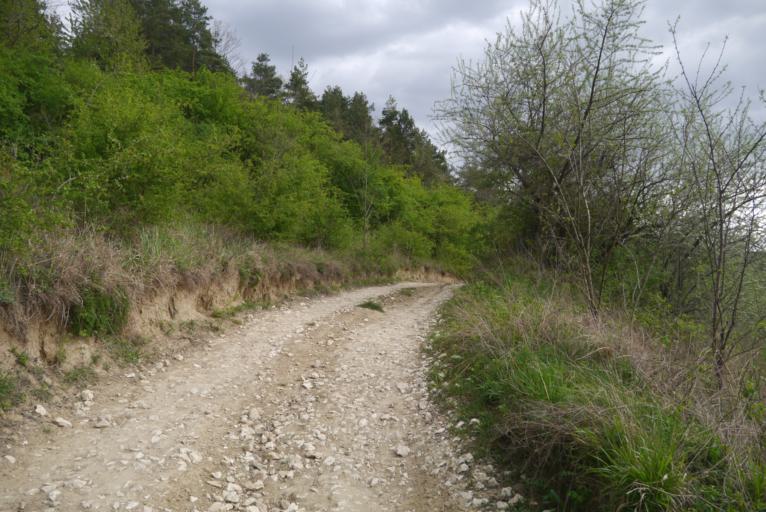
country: HU
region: Komarom-Esztergom
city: Piliscsev
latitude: 47.6724
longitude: 18.8317
